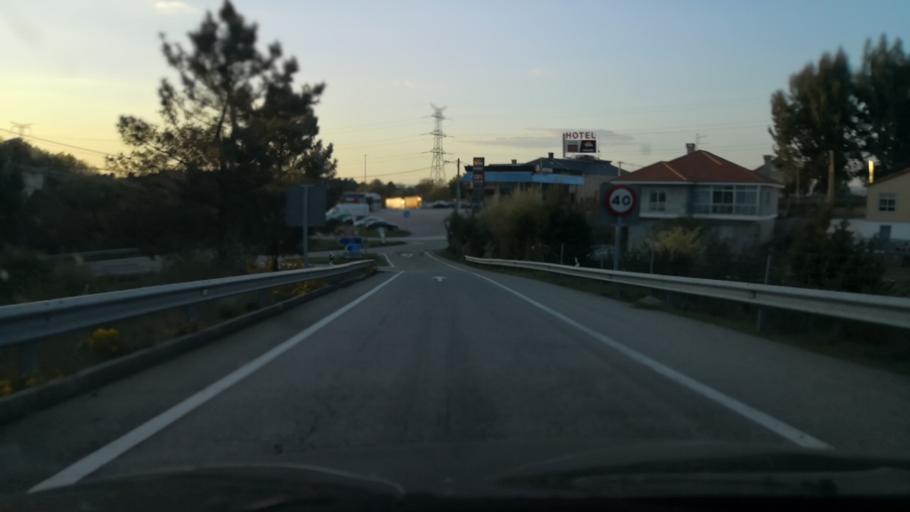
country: ES
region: Galicia
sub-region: Provincia de Ourense
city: Taboadela
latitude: 42.2496
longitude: -7.8634
